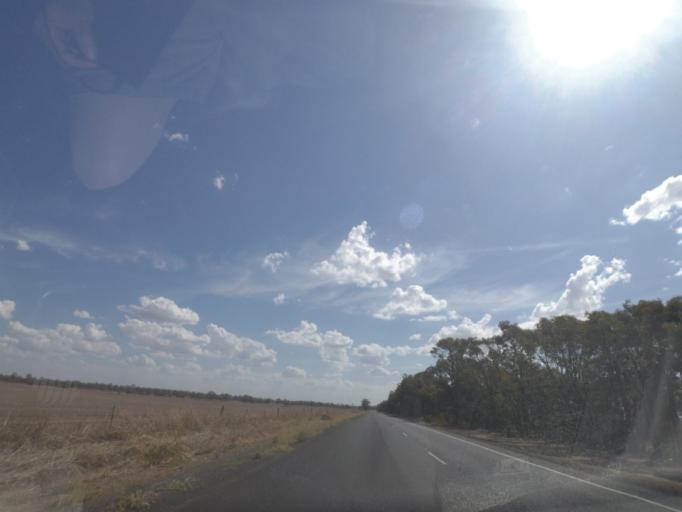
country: AU
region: Queensland
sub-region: Southern Downs
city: Stanthorpe
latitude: -28.4072
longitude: 151.1742
